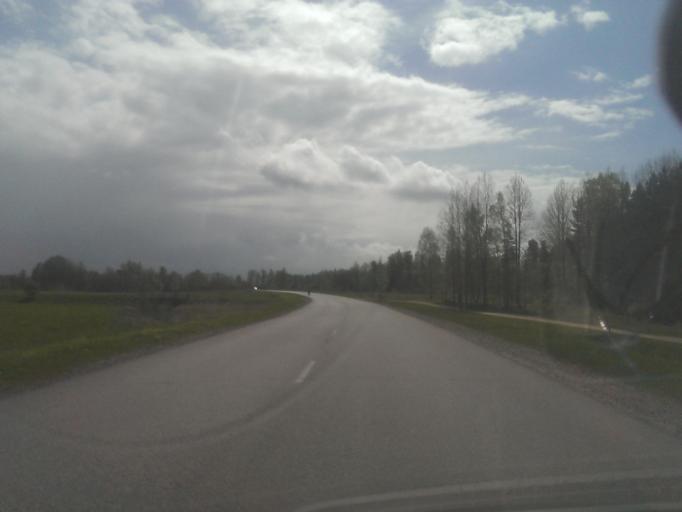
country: LV
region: Ventspils
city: Ventspils
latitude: 57.2892
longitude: 21.5658
